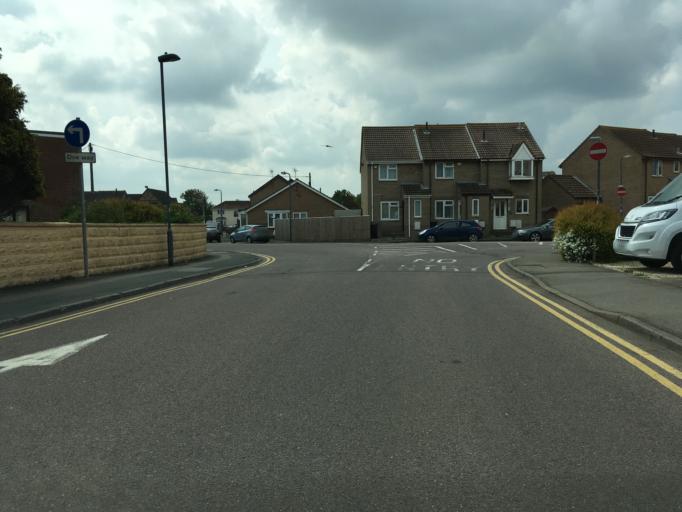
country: GB
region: England
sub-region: South Gloucestershire
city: Severn Beach
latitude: 51.5610
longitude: -2.6658
